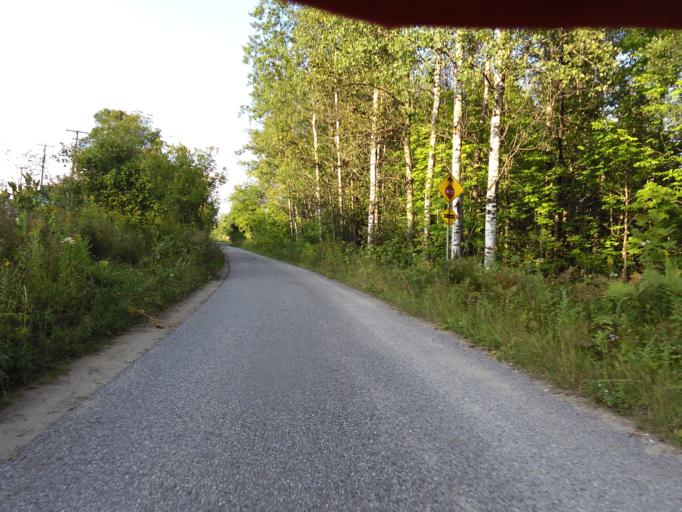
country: CA
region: Quebec
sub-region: Outaouais
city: Maniwaki
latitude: 46.3699
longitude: -75.9791
